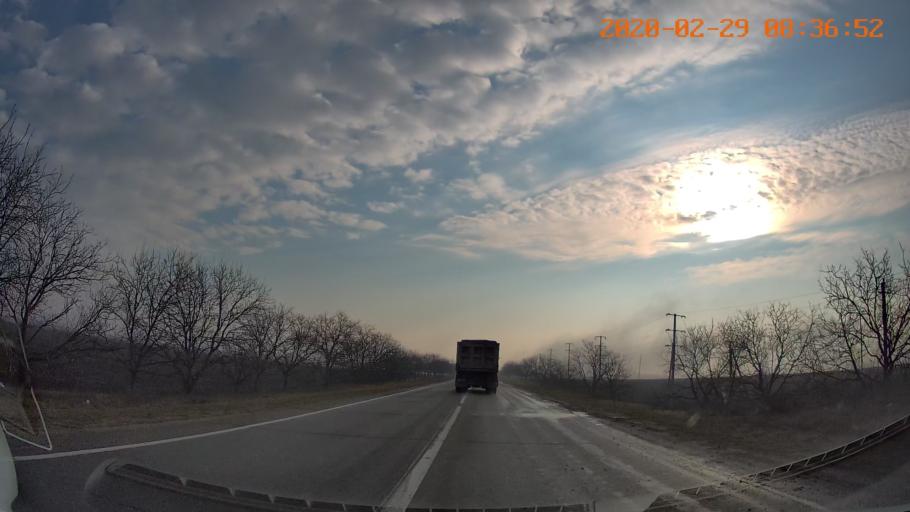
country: MD
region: Anenii Noi
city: Anenii Noi
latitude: 46.9215
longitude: 29.3529
